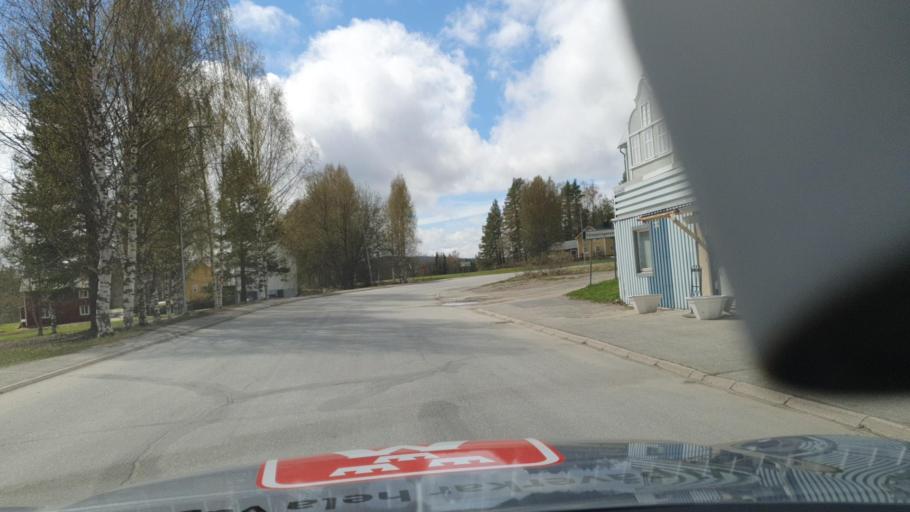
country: SE
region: Vaesterbotten
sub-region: Bjurholms Kommun
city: Bjurholm
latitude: 63.6926
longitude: 18.8645
